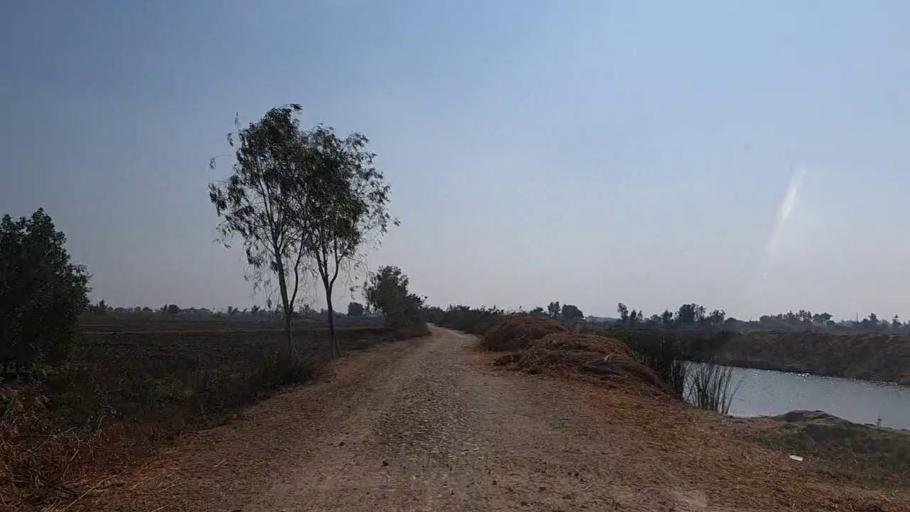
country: PK
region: Sindh
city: Thatta
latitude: 24.7963
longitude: 67.9685
